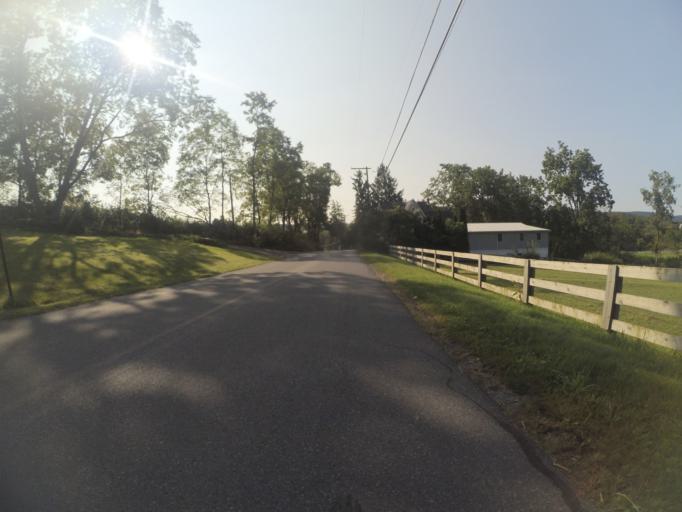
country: US
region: Pennsylvania
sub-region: Centre County
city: Boalsburg
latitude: 40.7985
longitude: -77.7622
